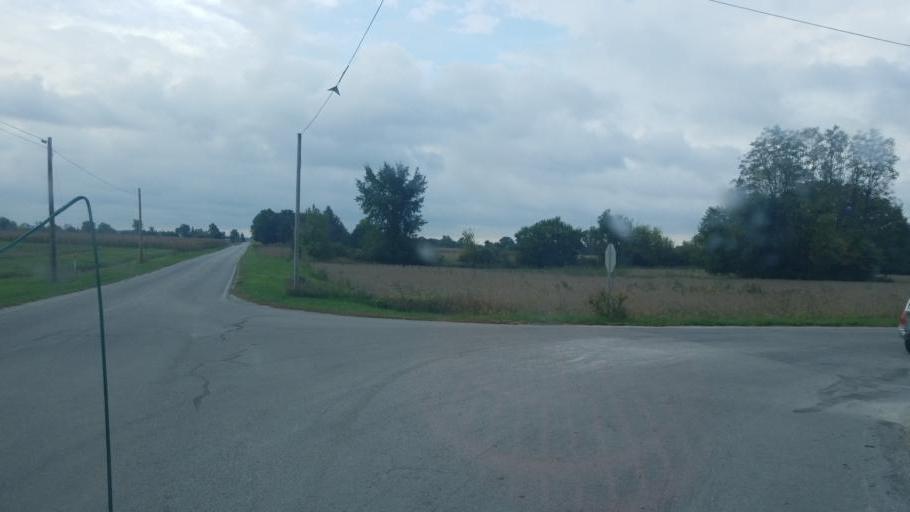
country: US
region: Ohio
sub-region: Wood County
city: North Baltimore
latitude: 41.1823
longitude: -83.6311
